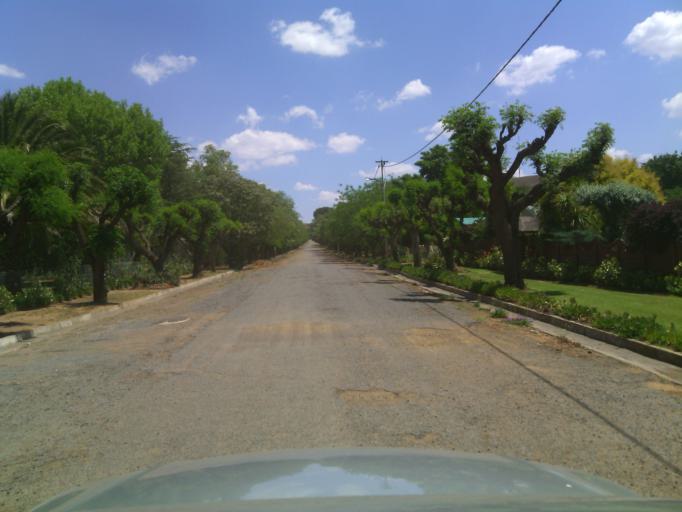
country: ZA
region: Orange Free State
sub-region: Xhariep District Municipality
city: Dewetsdorp
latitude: -29.5778
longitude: 26.6673
